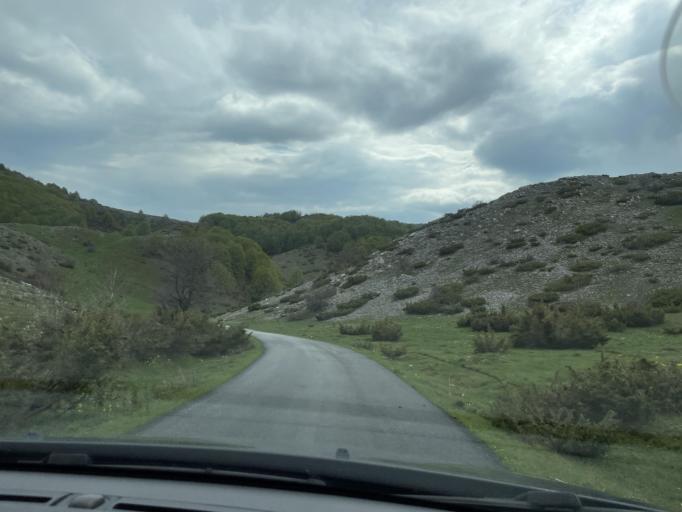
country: MK
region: Opstina Rostusa
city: Rostusha
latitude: 41.6025
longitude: 20.6841
